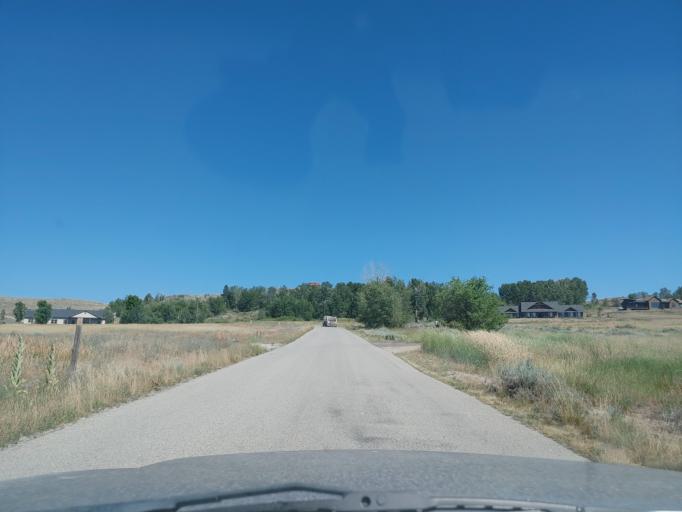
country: US
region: Montana
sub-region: Ravalli County
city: Hamilton
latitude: 46.3484
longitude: -114.0583
